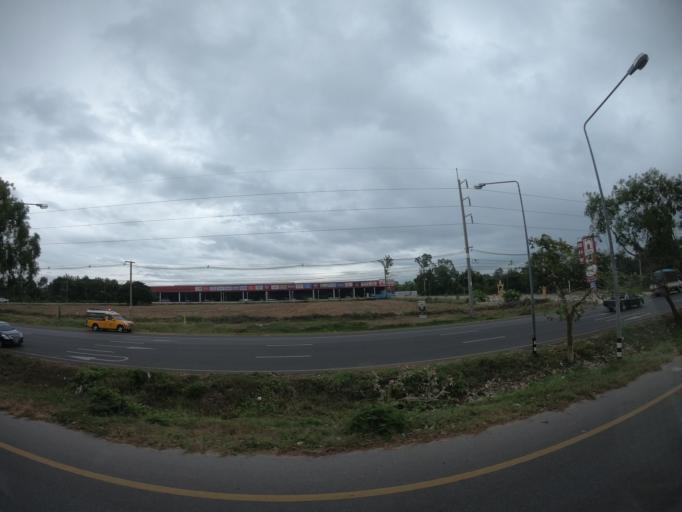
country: TH
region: Roi Et
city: Roi Et
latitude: 16.0553
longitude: 103.6200
